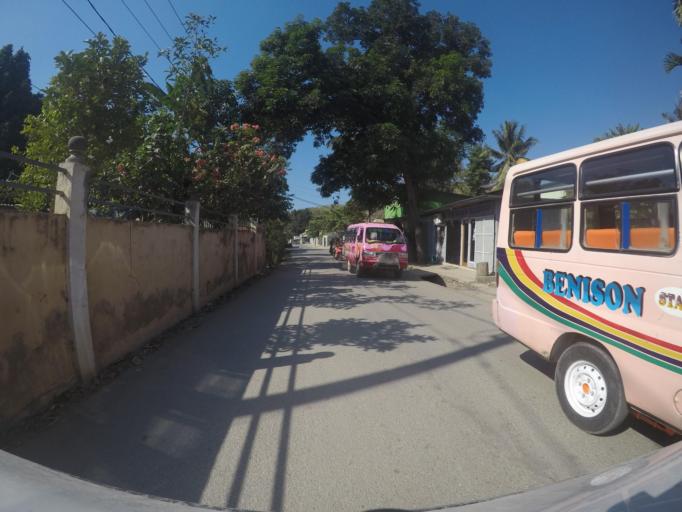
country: TL
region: Dili
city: Dili
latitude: -8.5746
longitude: 125.5419
